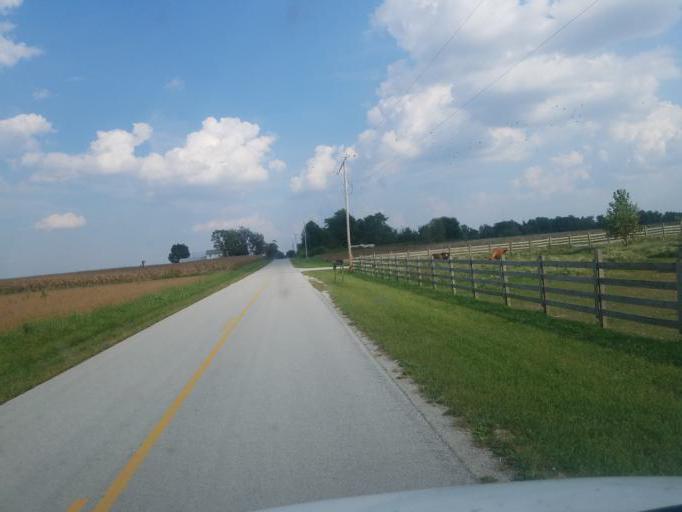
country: US
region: Ohio
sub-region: Hancock County
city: Arlington
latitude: 40.8124
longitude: -83.6669
